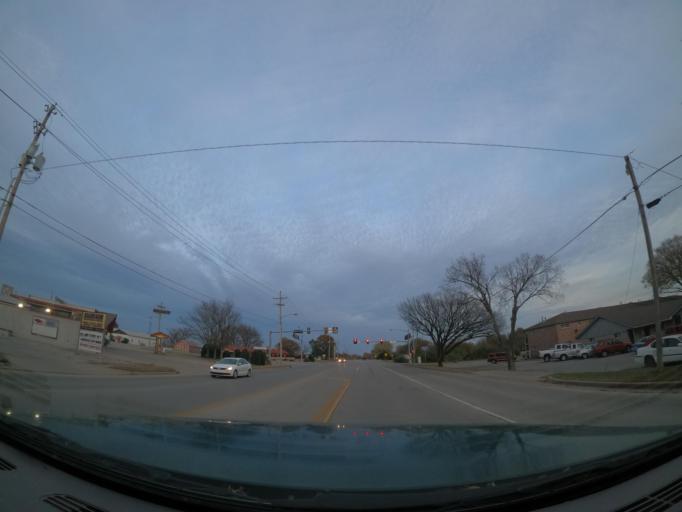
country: US
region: Oklahoma
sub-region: Tulsa County
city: Broken Arrow
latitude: 36.0319
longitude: -95.7916
